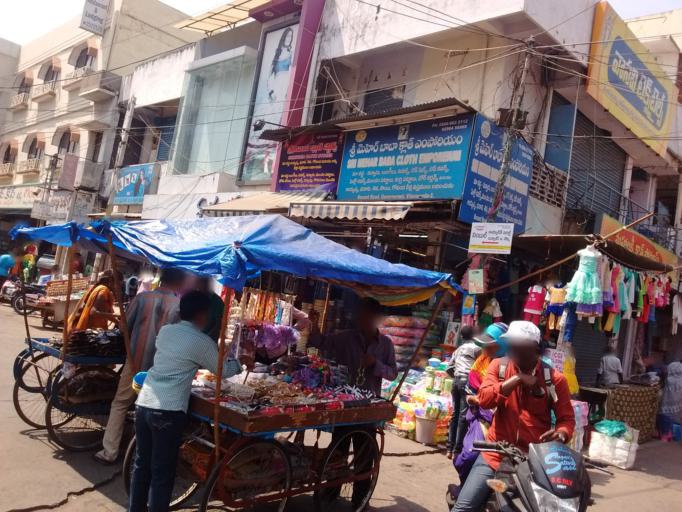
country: IN
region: Andhra Pradesh
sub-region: Krishna
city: Vijayawada
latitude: 16.5128
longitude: 80.6270
